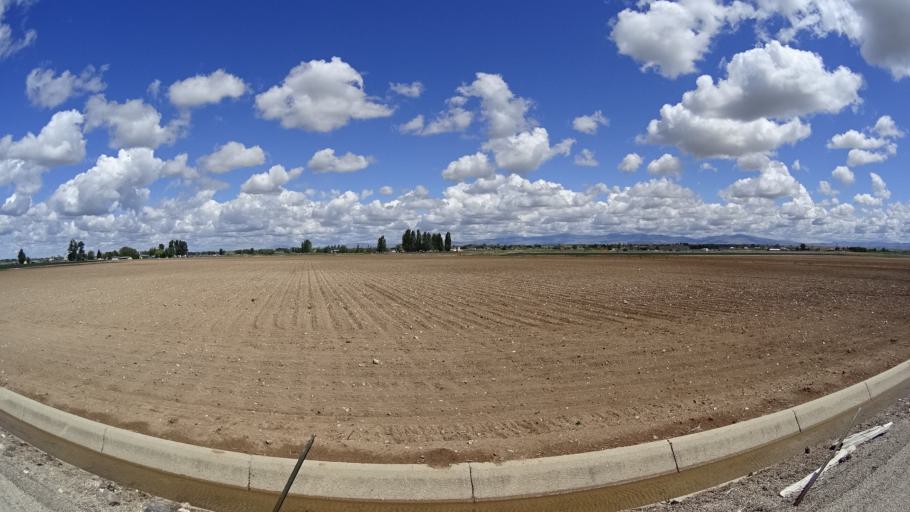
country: US
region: Idaho
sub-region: Ada County
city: Kuna
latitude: 43.4614
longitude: -116.3714
